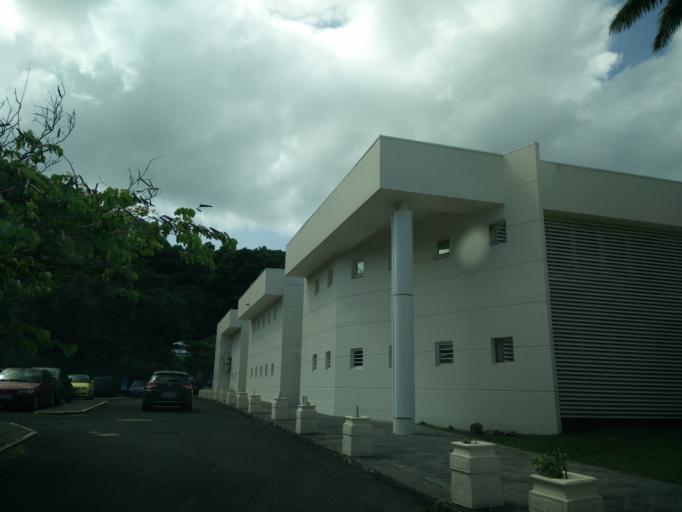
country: GP
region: Guadeloupe
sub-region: Guadeloupe
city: Basse-Terre
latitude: 15.9862
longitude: -61.7102
